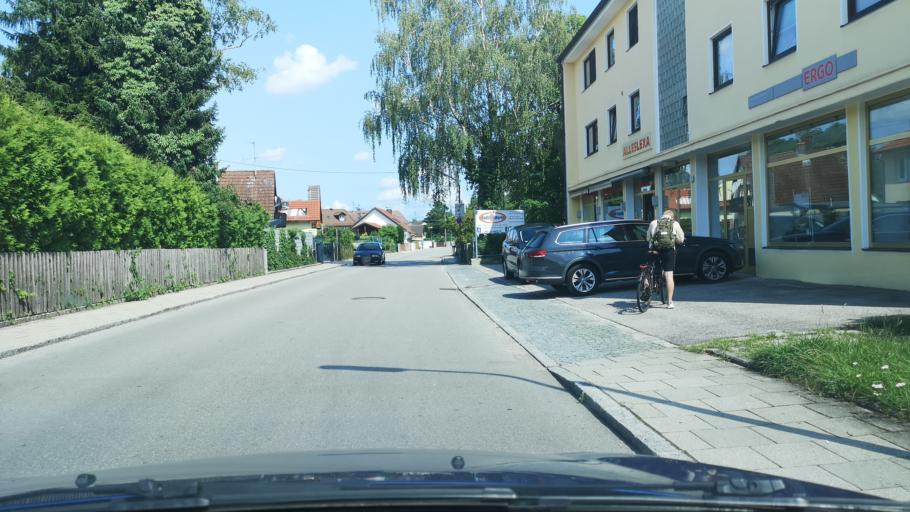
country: DE
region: Bavaria
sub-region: Upper Bavaria
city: Kirchheim bei Muenchen
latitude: 48.1593
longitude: 11.7568
